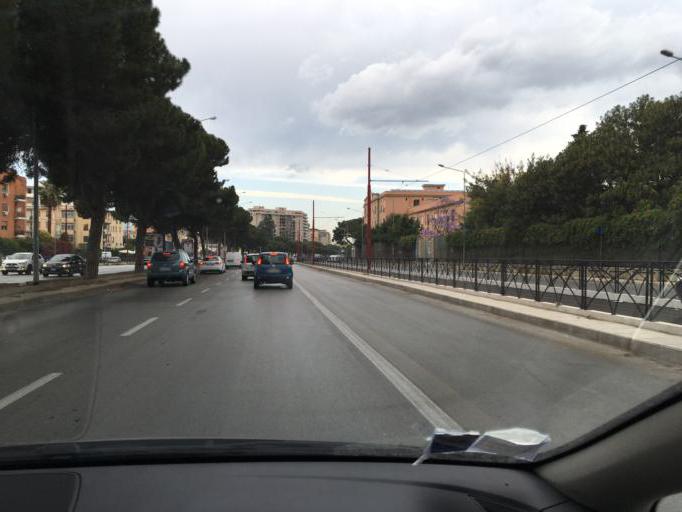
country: IT
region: Sicily
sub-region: Palermo
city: Palermo
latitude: 38.1176
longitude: 13.3291
